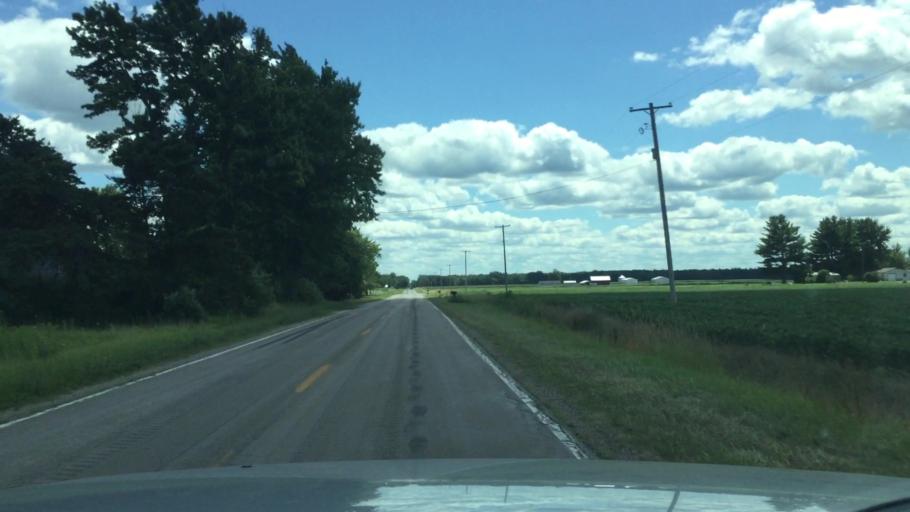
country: US
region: Michigan
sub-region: Saginaw County
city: Saint Charles
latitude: 43.3441
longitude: -84.1899
